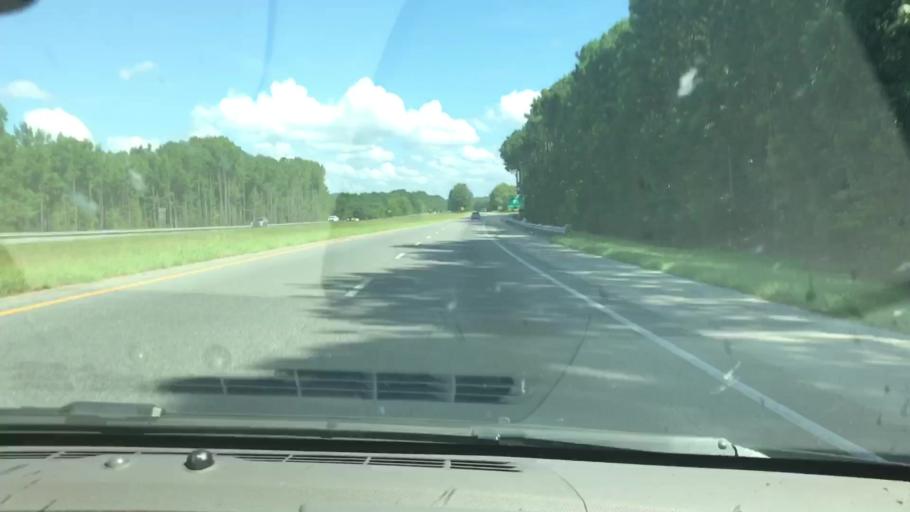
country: US
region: Georgia
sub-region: Harris County
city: Hamilton
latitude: 32.7411
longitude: -85.0191
